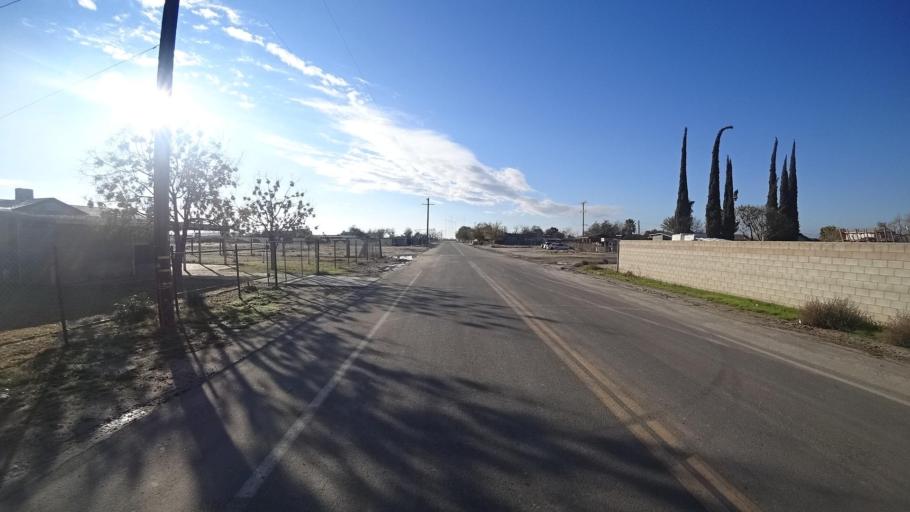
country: US
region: California
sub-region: Kern County
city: Delano
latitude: 35.7720
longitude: -119.2830
